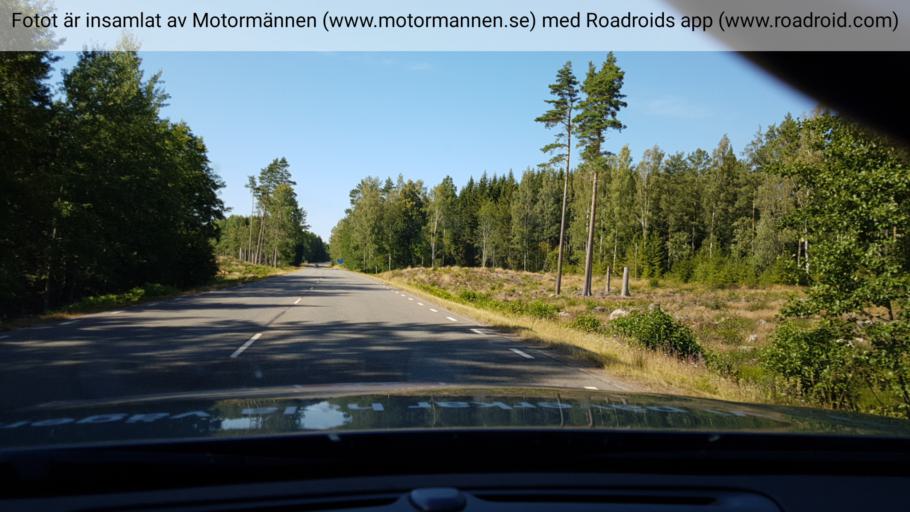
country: SE
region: Vaestra Goetaland
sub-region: Karlsborgs Kommun
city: Molltorp
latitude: 58.6017
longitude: 14.3983
